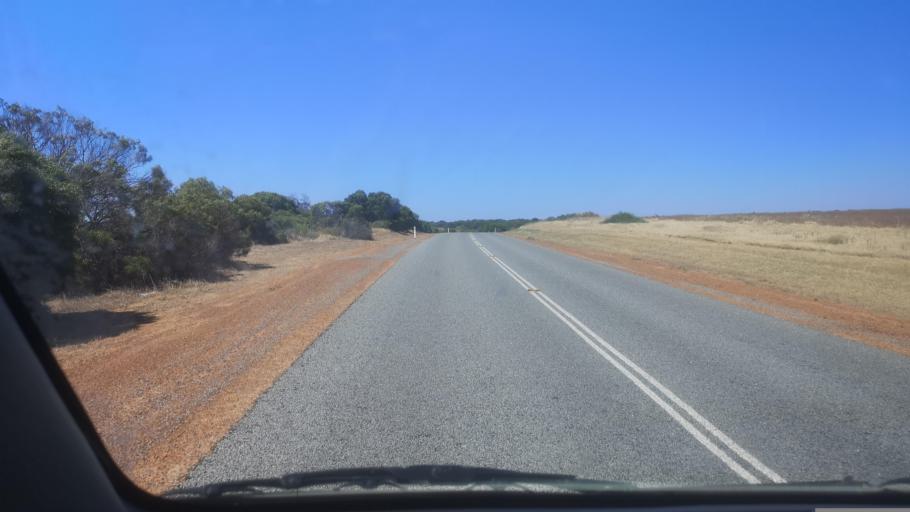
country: AU
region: Western Australia
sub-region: Northampton Shire
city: Kalbarri
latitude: -28.0182
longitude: 114.1979
